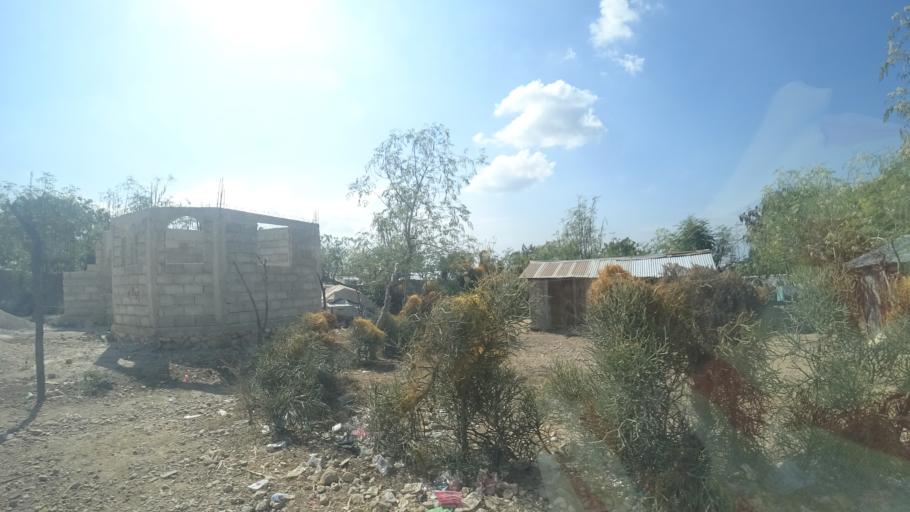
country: HT
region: Ouest
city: Croix des Bouquets
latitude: 18.6594
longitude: -72.2879
